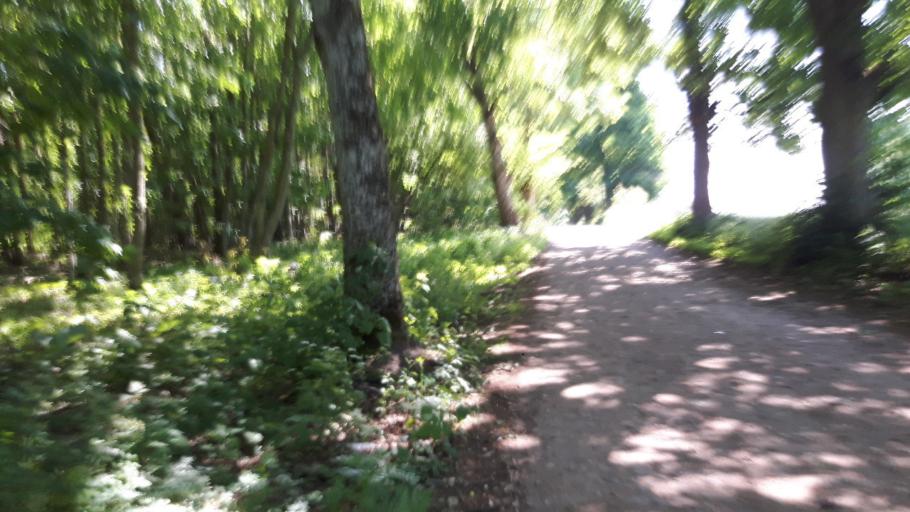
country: PL
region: Pomeranian Voivodeship
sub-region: Powiat wejherowski
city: Choczewo
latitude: 54.7376
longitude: 17.9484
